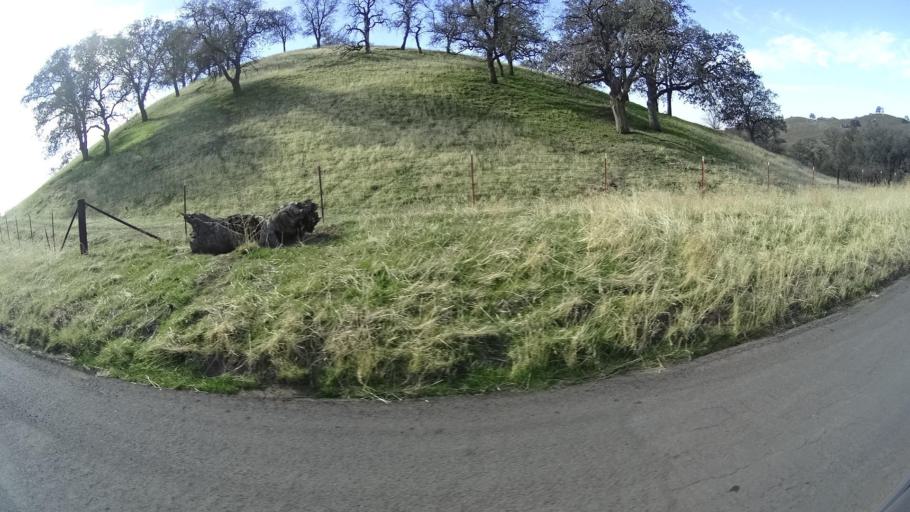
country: US
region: California
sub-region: Tulare County
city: Richgrove
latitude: 35.6608
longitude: -118.8439
